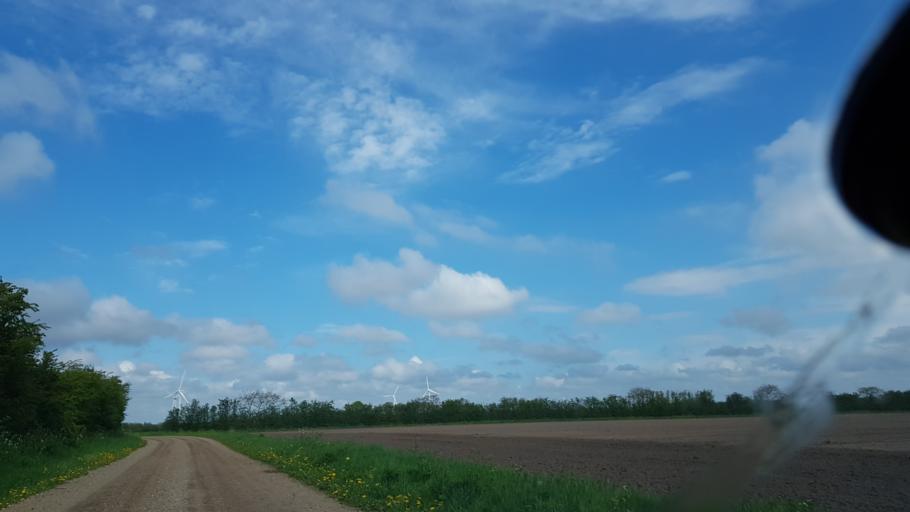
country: DK
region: South Denmark
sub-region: Tonder Kommune
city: Sherrebek
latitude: 55.0887
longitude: 8.8483
